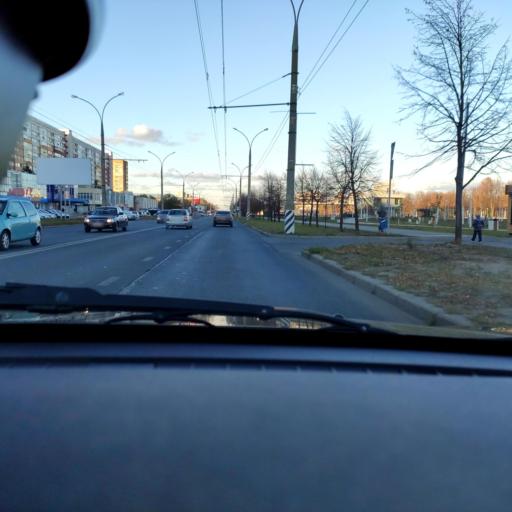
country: RU
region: Samara
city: Tol'yatti
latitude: 53.5113
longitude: 49.2719
